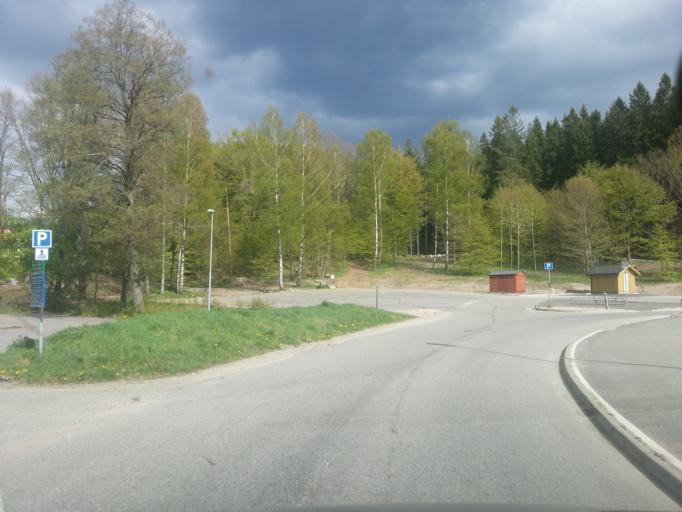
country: SE
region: Vaestra Goetaland
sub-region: Lerums Kommun
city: Lerum
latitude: 57.7594
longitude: 12.2810
